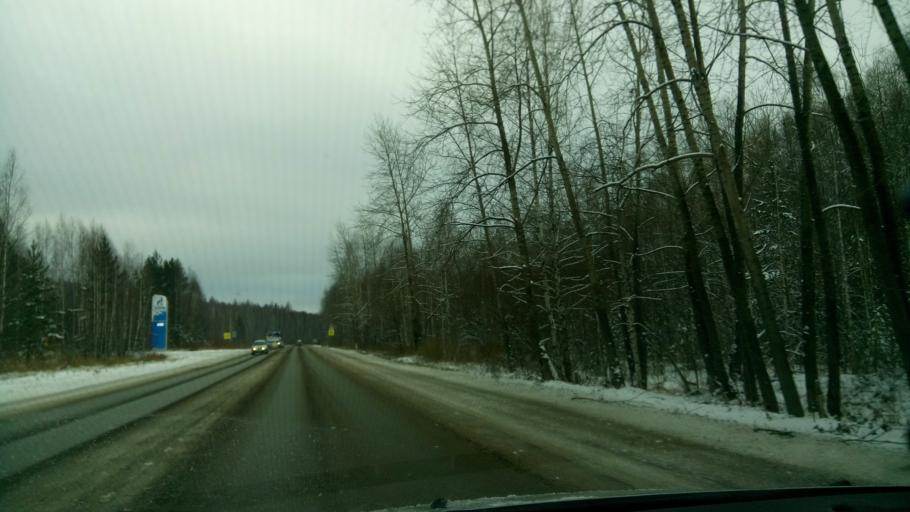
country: RU
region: Sverdlovsk
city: Polevskoy
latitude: 56.4670
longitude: 60.2256
